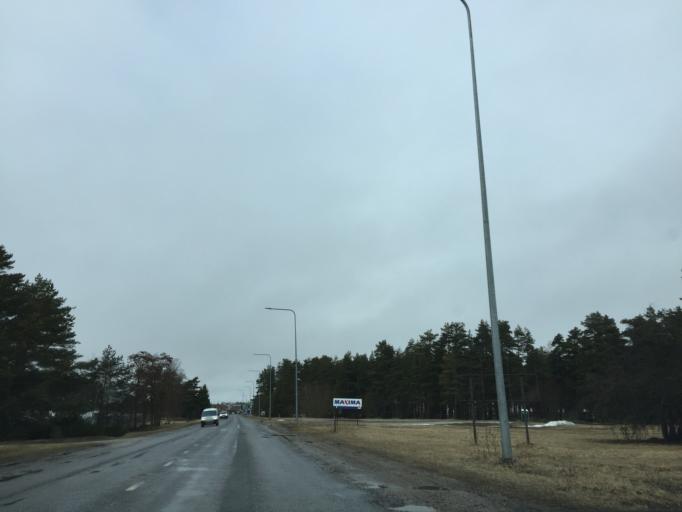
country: EE
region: Laeaene
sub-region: Haapsalu linn
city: Haapsalu
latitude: 58.9225
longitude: 23.5477
